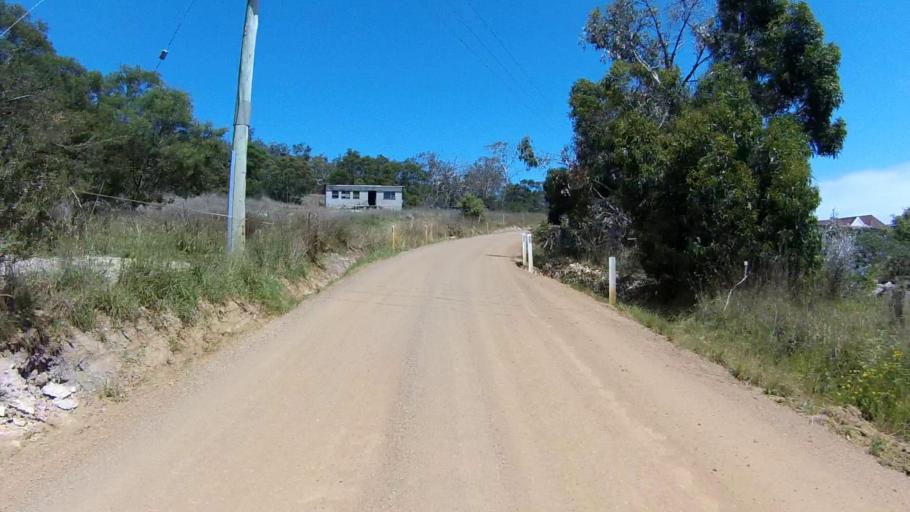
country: AU
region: Tasmania
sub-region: Clarence
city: Lauderdale
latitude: -42.9322
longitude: 147.4672
